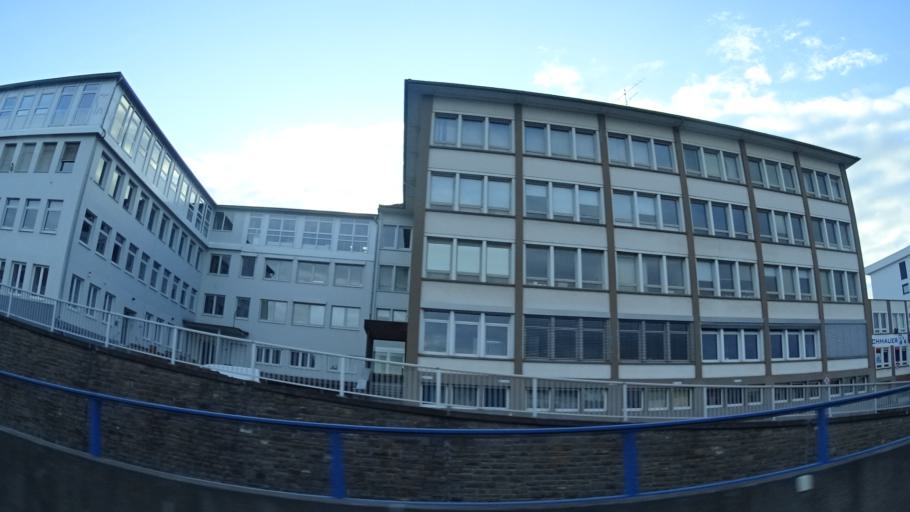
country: DE
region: Rheinland-Pfalz
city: Bingen am Rhein
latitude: 49.9622
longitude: 7.8903
